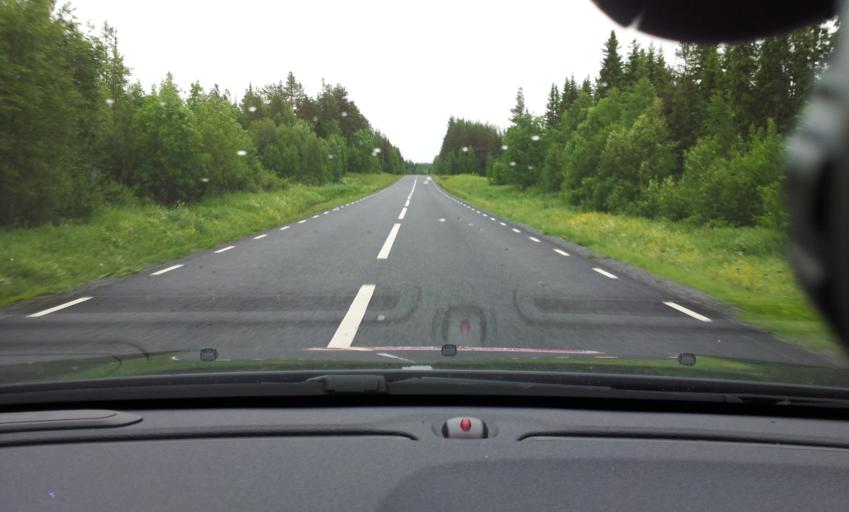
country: SE
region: Jaemtland
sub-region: Stroemsunds Kommun
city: Stroemsund
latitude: 63.6666
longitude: 15.1337
